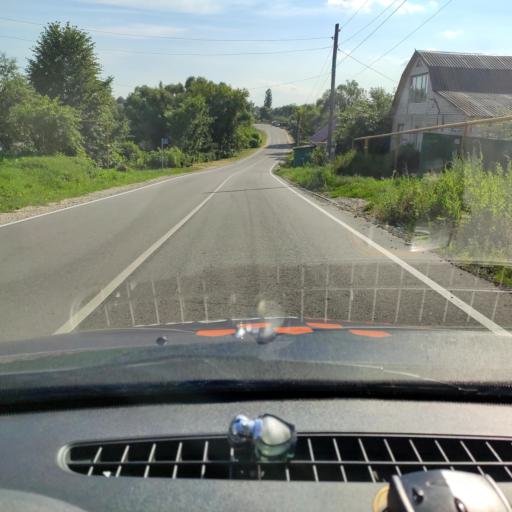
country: RU
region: Voronezj
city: Devitsa
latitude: 51.6461
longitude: 38.9653
